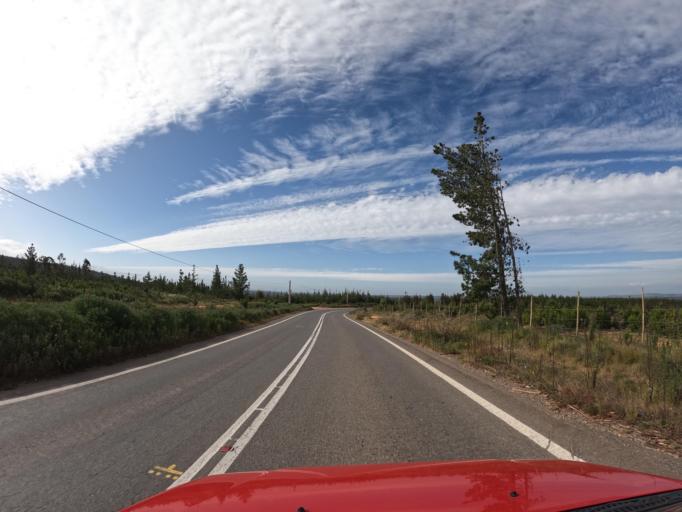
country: CL
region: O'Higgins
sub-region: Provincia de Colchagua
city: Santa Cruz
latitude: -34.3065
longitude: -71.8353
